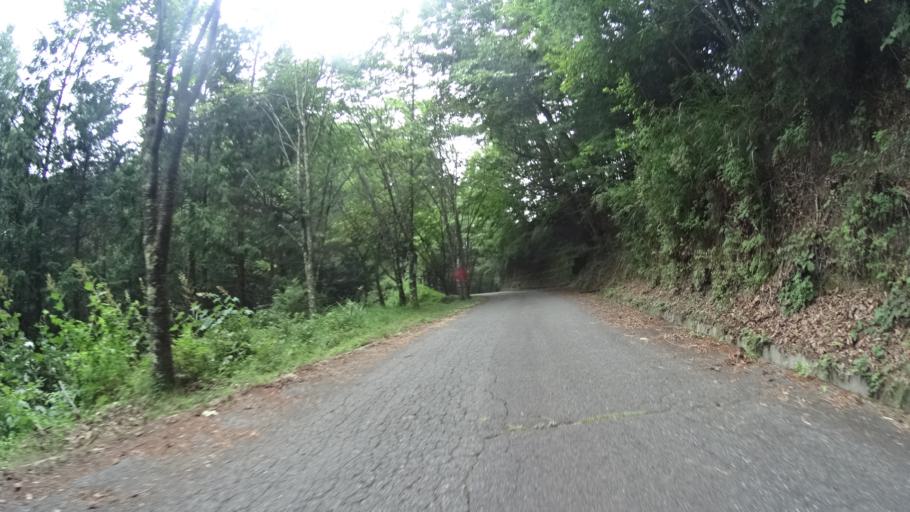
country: JP
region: Yamanashi
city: Kofu-shi
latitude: 35.8098
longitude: 138.5916
